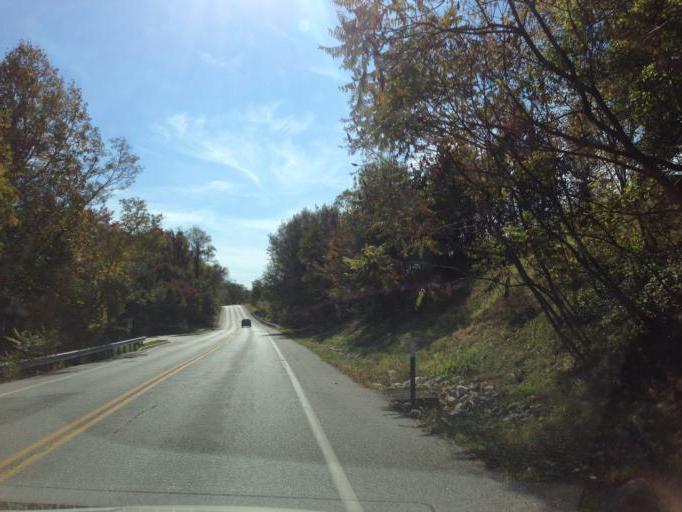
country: US
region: Maryland
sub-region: Howard County
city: Ellicott City
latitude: 39.2626
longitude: -76.8192
